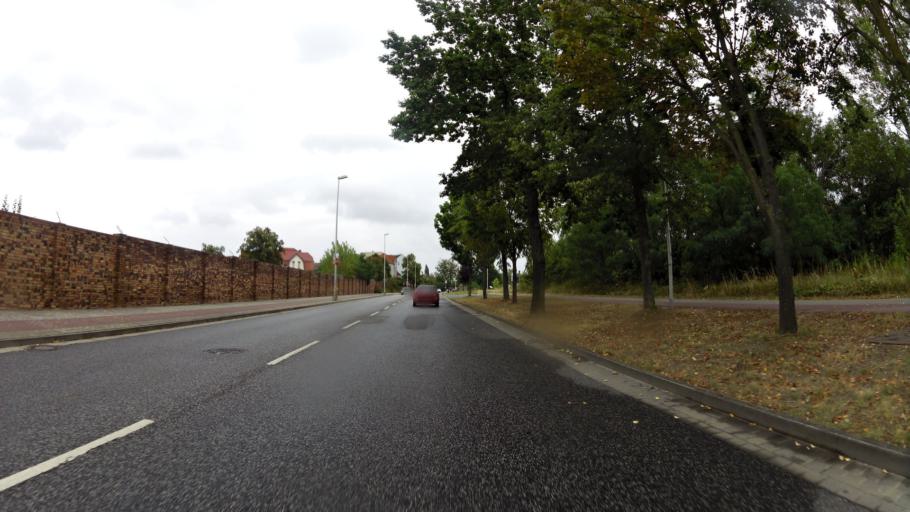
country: DE
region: Brandenburg
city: Cottbus
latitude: 51.7545
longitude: 14.3191
